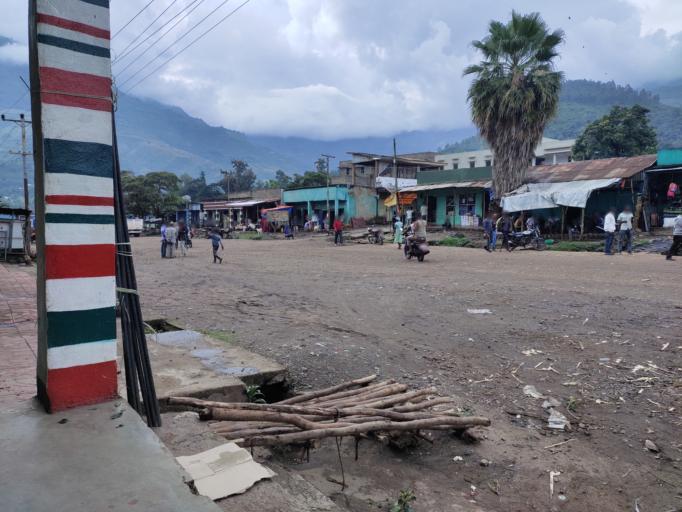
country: ET
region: Southern Nations, Nationalities, and People's Region
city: Felege Neway
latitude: 6.3009
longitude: 36.8809
